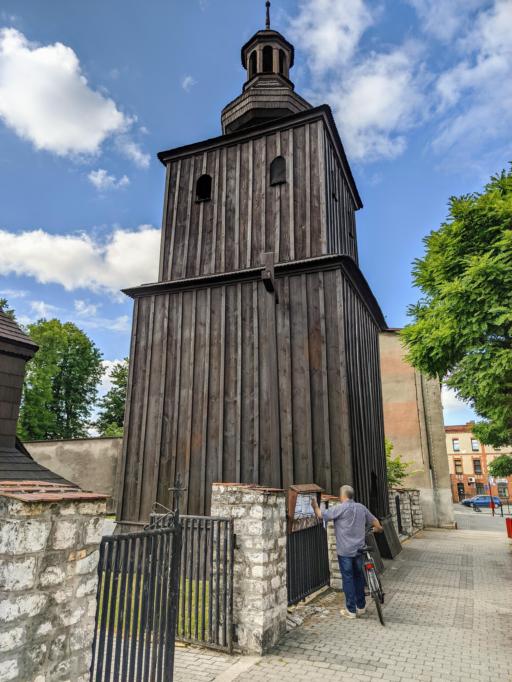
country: PL
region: Silesian Voivodeship
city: Miasteczko Slaskie
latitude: 50.4921
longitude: 18.9230
